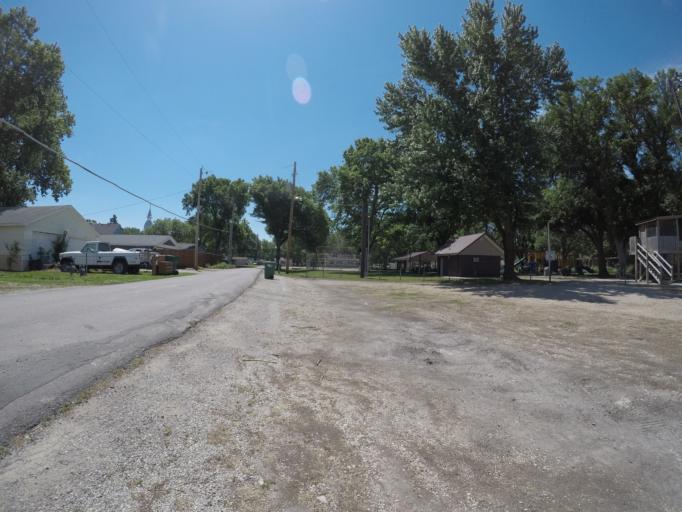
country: US
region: Kansas
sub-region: Wabaunsee County
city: Alma
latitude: 39.0544
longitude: -96.2398
